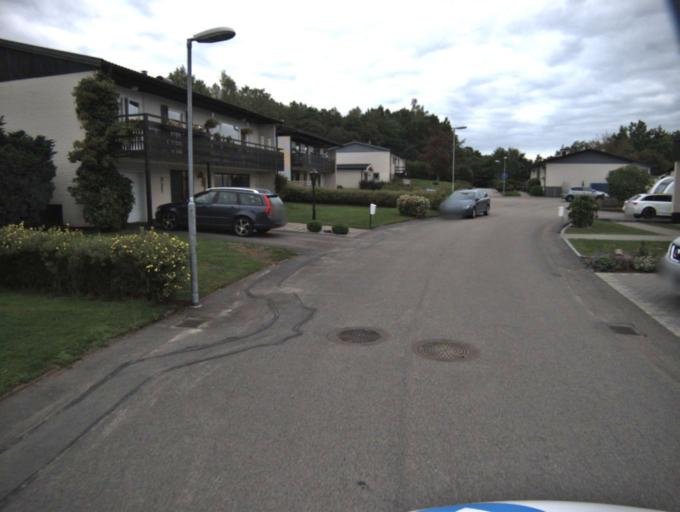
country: SE
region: Vaestra Goetaland
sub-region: Ulricehamns Kommun
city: Ulricehamn
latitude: 57.7965
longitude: 13.4275
